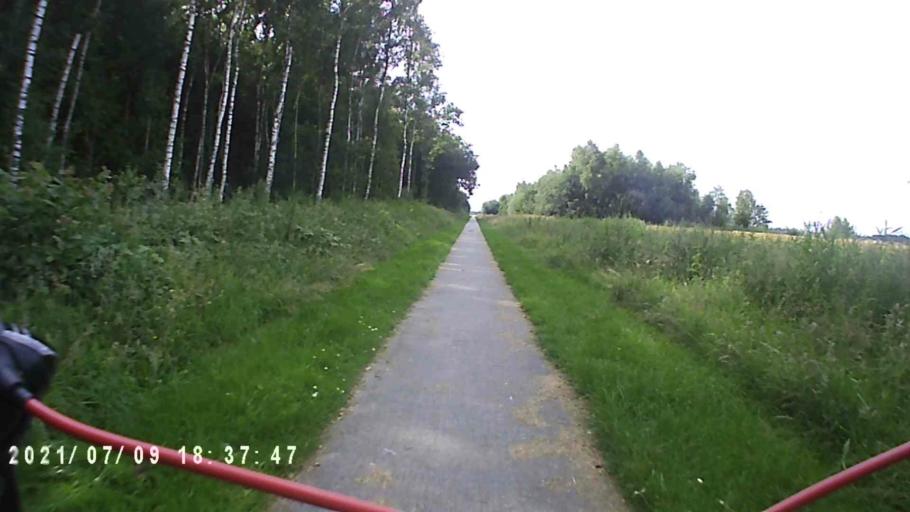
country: NL
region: Groningen
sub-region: Gemeente Pekela
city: Oude Pekela
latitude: 53.0779
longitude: 6.9512
